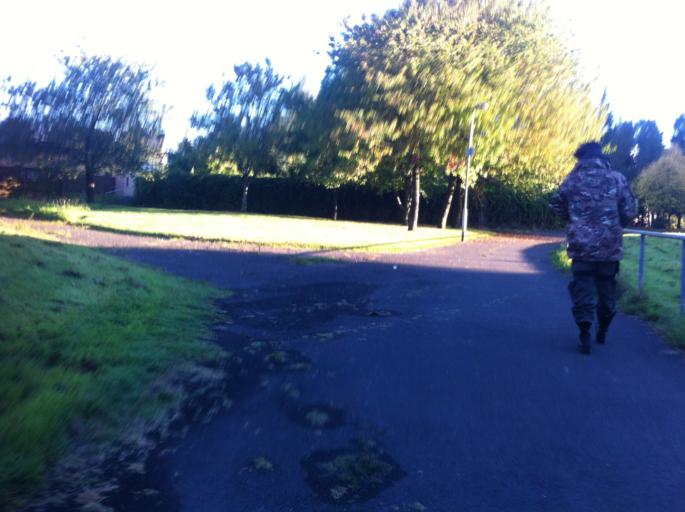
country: GB
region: Scotland
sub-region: Glasgow City
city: Glasgow
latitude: 55.8721
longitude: -4.2399
